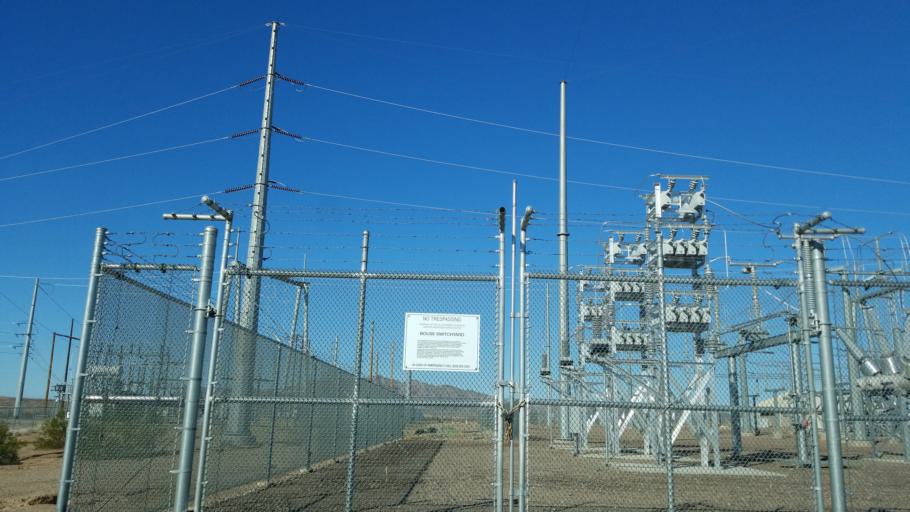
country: US
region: Arizona
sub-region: La Paz County
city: Parker
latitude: 33.9981
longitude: -114.2157
